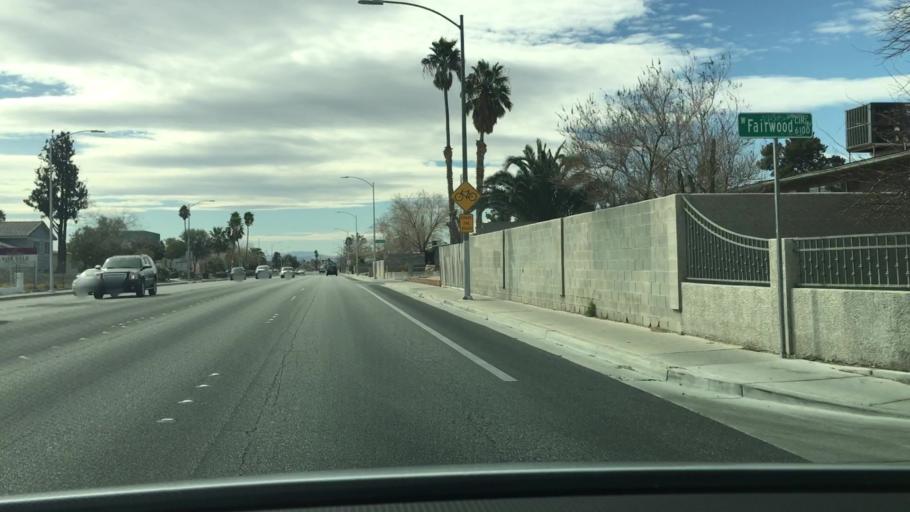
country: US
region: Nevada
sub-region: Clark County
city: Spring Valley
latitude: 36.1710
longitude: -115.2241
